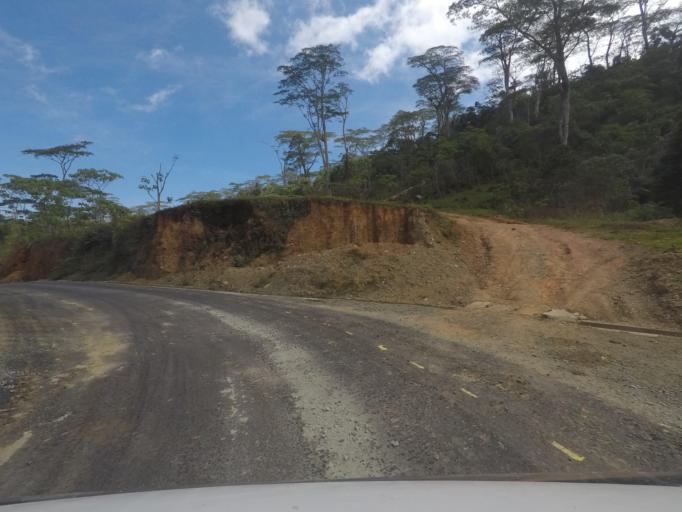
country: TL
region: Ermera
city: Gleno
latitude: -8.7470
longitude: 125.3427
